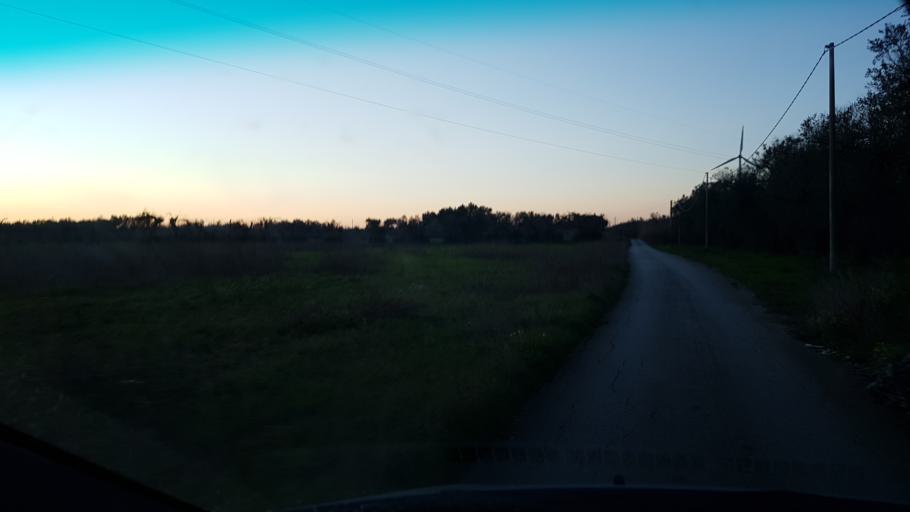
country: IT
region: Apulia
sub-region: Provincia di Brindisi
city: San Pietro Vernotico
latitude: 40.5005
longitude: 17.9816
